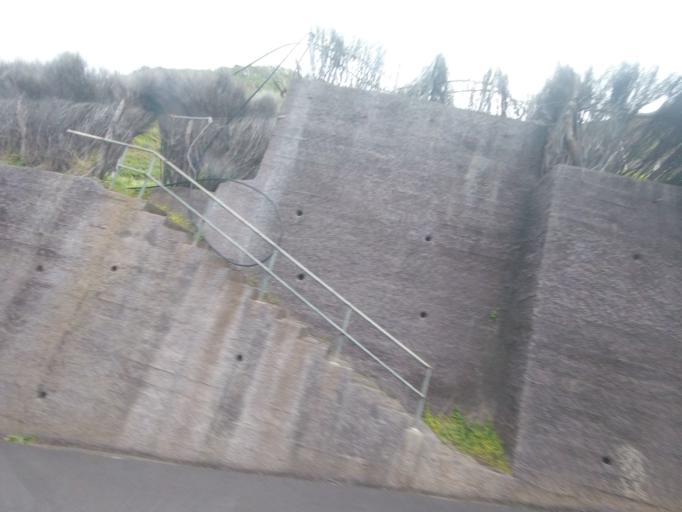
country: PT
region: Madeira
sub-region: Porto Moniz
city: Porto Moniz
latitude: 32.8550
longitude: -17.1555
